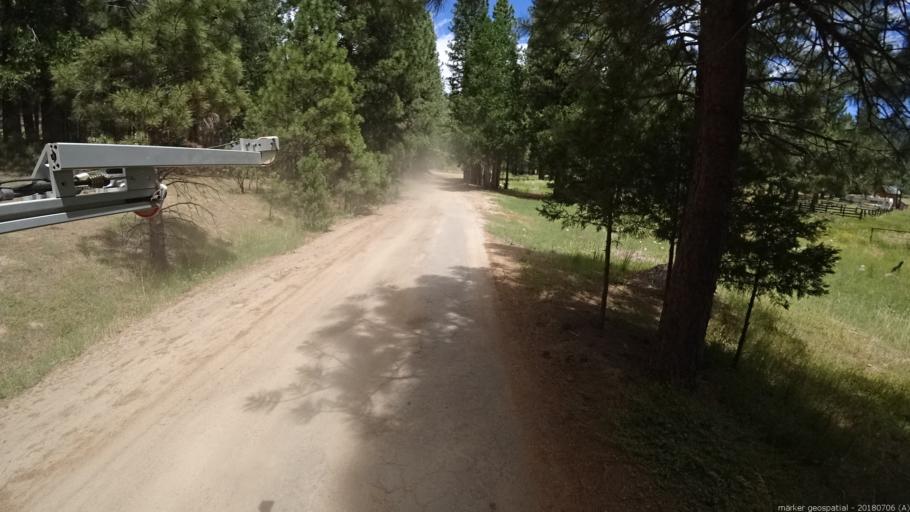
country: US
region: California
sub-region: Madera County
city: Oakhurst
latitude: 37.4160
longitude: -119.3709
